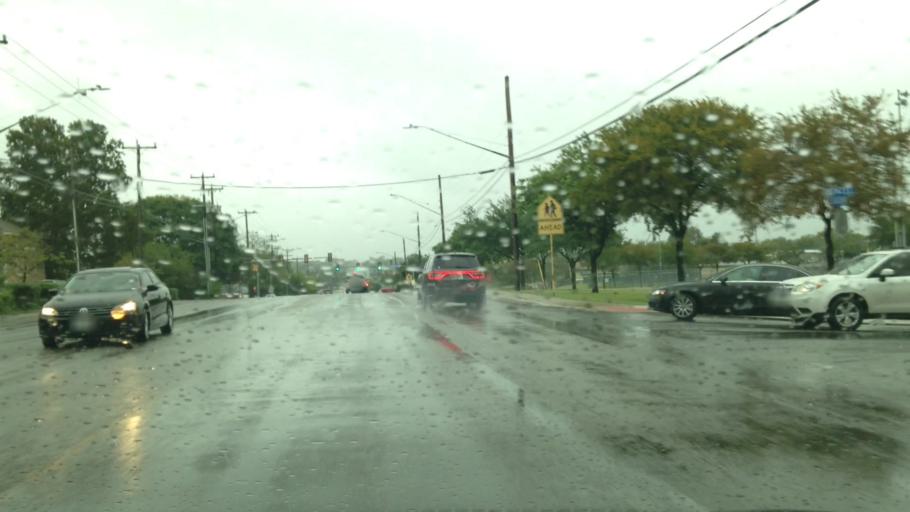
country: US
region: Texas
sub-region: Bexar County
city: Live Oak
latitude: 29.5738
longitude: -98.3697
